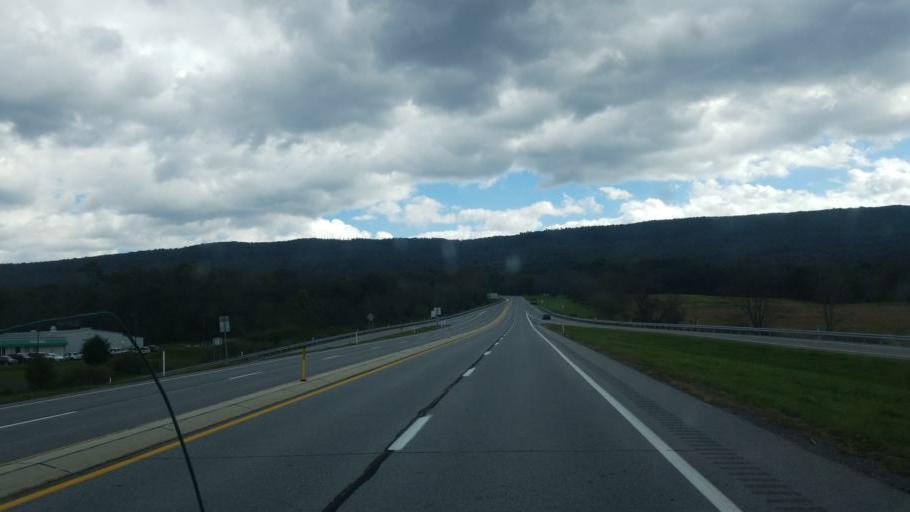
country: US
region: Pennsylvania
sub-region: Fulton County
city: McConnellsburg
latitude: 39.9434
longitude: -77.9923
